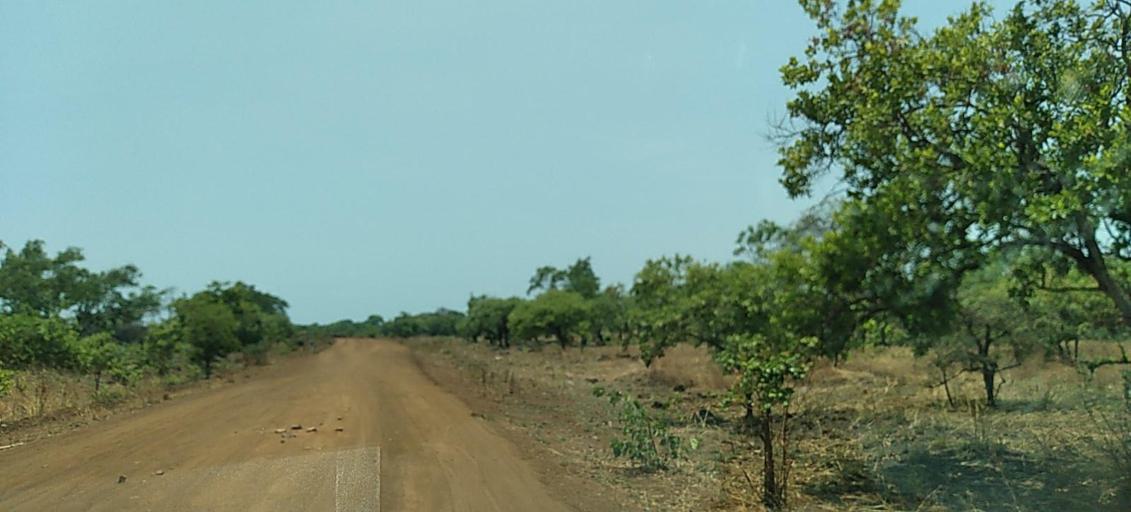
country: ZM
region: Copperbelt
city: Mpongwe
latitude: -13.7041
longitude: 27.8681
